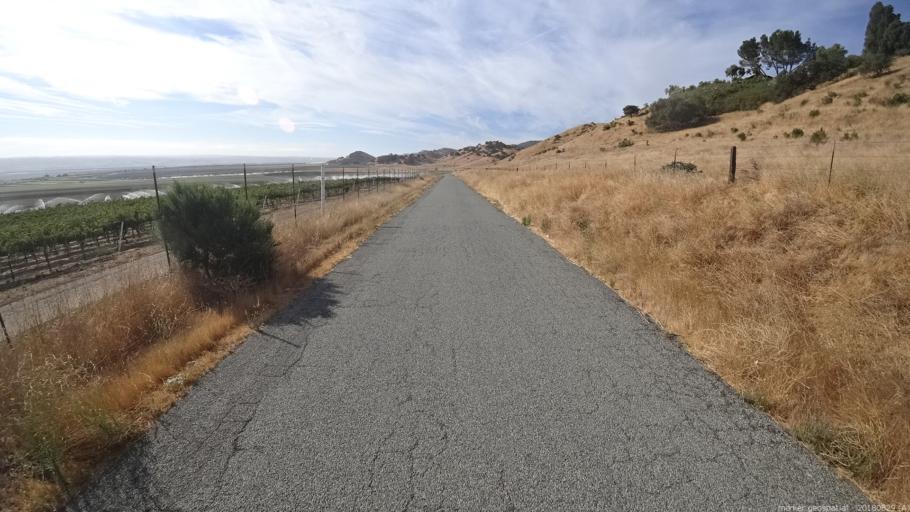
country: US
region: California
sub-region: Monterey County
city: King City
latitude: 36.0152
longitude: -120.9365
